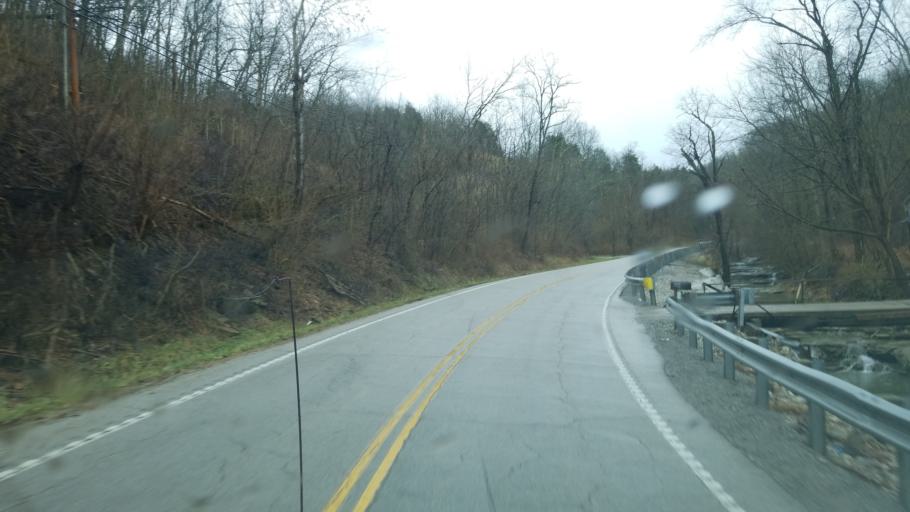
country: US
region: Kentucky
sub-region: Mason County
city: Maysville
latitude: 38.6159
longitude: -83.6969
